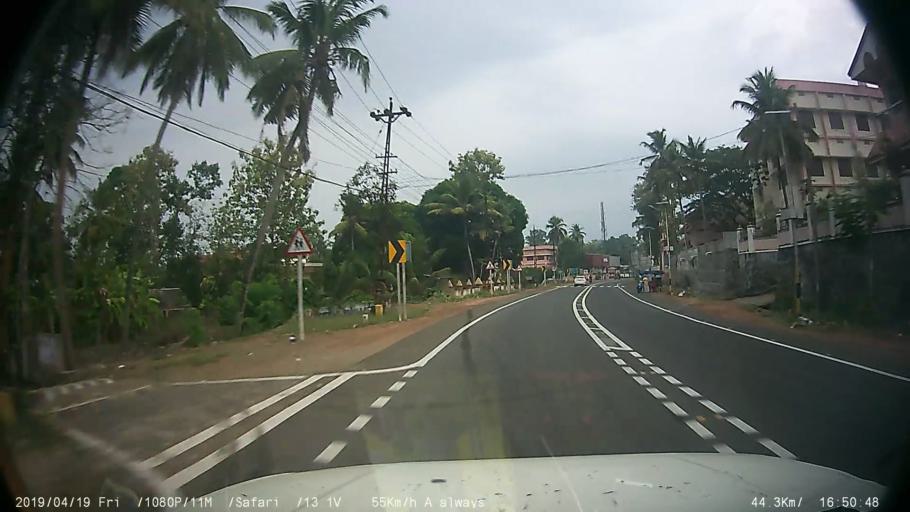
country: IN
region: Kerala
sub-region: Kottayam
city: Changanacheri
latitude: 9.4614
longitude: 76.5330
